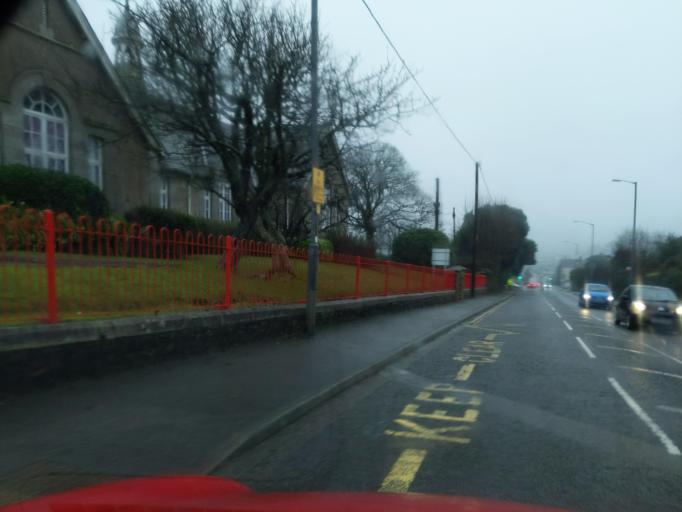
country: GB
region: England
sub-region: Cornwall
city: Callington
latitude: 50.5008
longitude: -4.3132
